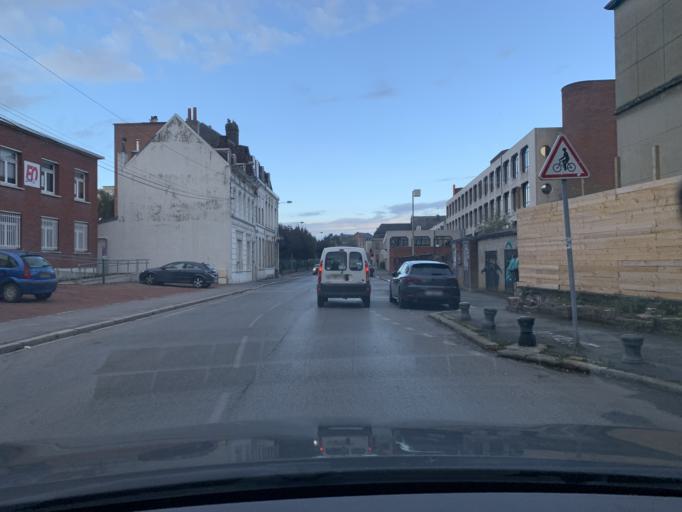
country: FR
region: Nord-Pas-de-Calais
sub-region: Departement du Nord
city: Neuville-Saint-Remy
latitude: 50.1779
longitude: 3.2281
